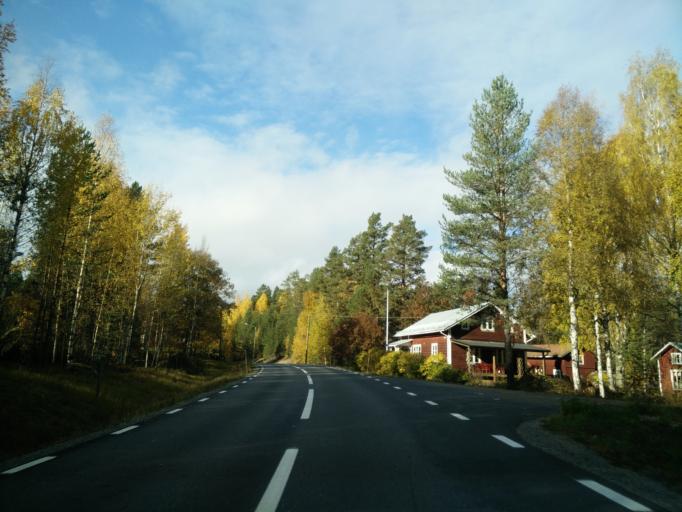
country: SE
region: Jaemtland
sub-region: Braecke Kommun
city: Braecke
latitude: 62.3918
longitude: 15.0793
